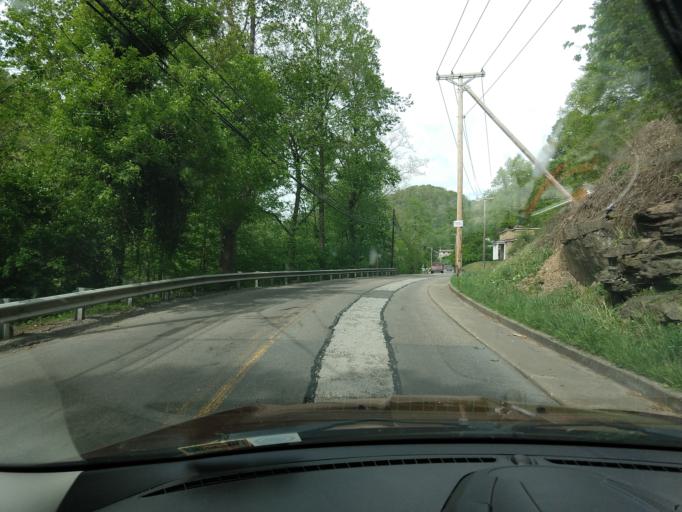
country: US
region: West Virginia
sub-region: McDowell County
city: Welch
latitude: 37.4208
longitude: -81.5884
